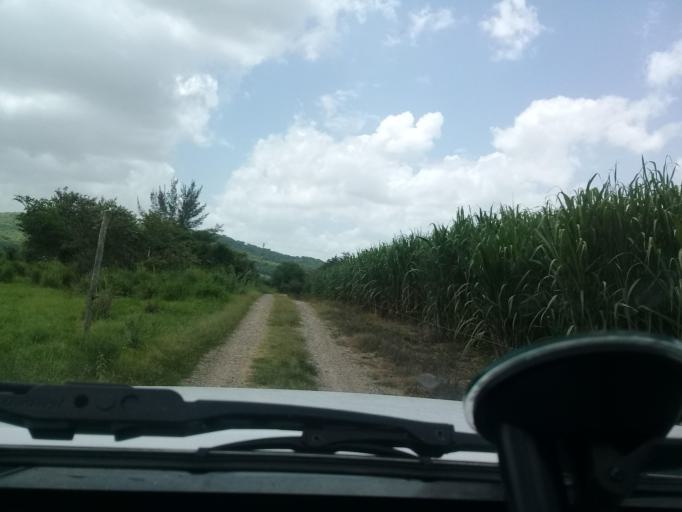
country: MX
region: Veracruz
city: Moralillo
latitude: 22.1336
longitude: -98.0334
